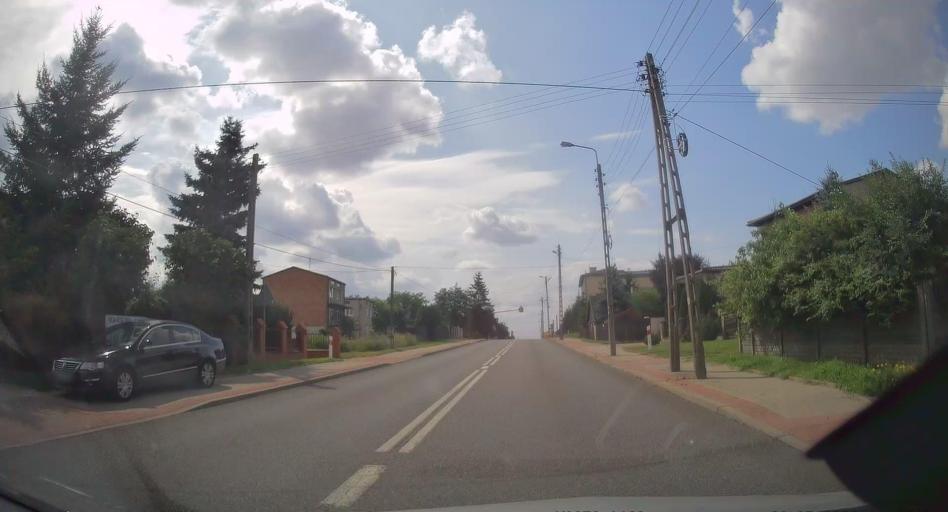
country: PL
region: Lodz Voivodeship
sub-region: Powiat brzezinski
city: Jezow
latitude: 51.8127
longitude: 19.9751
